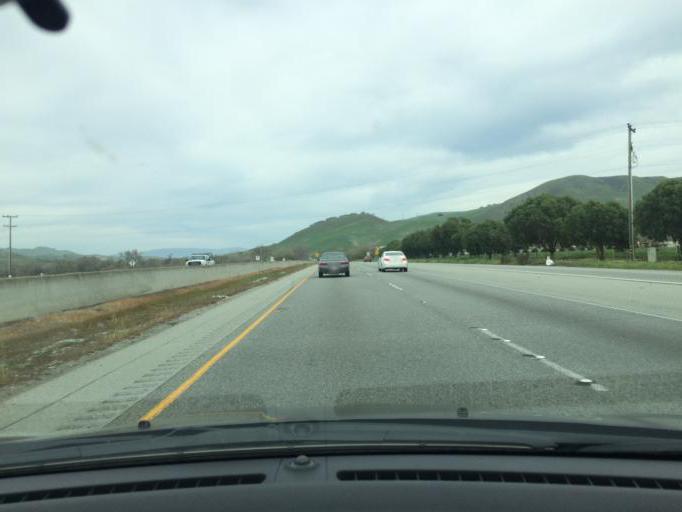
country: US
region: California
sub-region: San Benito County
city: San Juan Bautista
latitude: 36.8832
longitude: -121.5610
